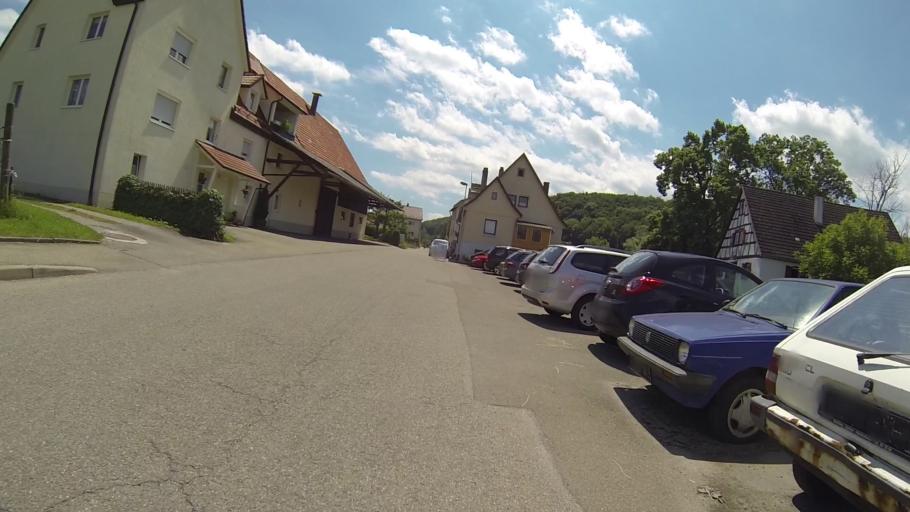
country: DE
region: Baden-Wuerttemberg
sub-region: Regierungsbezirk Stuttgart
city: Herbrechtingen
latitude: 48.6166
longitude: 10.1766
